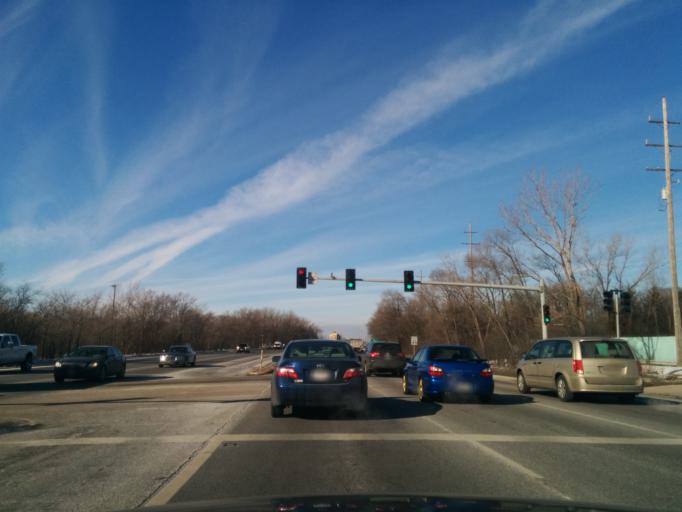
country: US
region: Illinois
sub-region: DuPage County
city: Elmhurst
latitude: 41.8995
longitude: -87.9643
